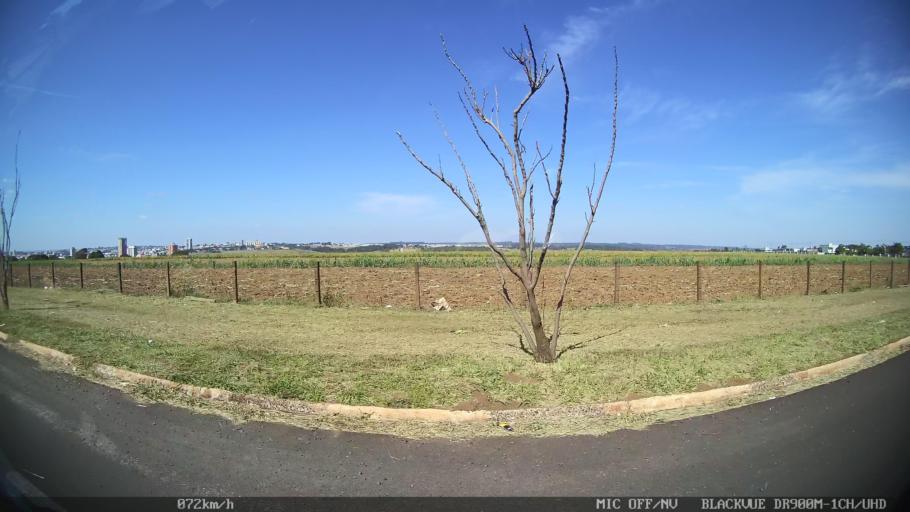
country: BR
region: Sao Paulo
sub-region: Franca
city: Franca
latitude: -20.5502
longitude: -47.4296
